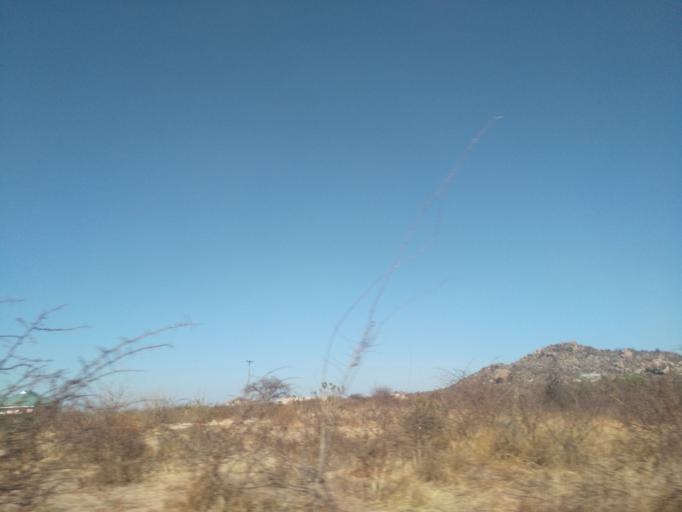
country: TZ
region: Dodoma
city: Dodoma
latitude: -6.1763
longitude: 35.7012
